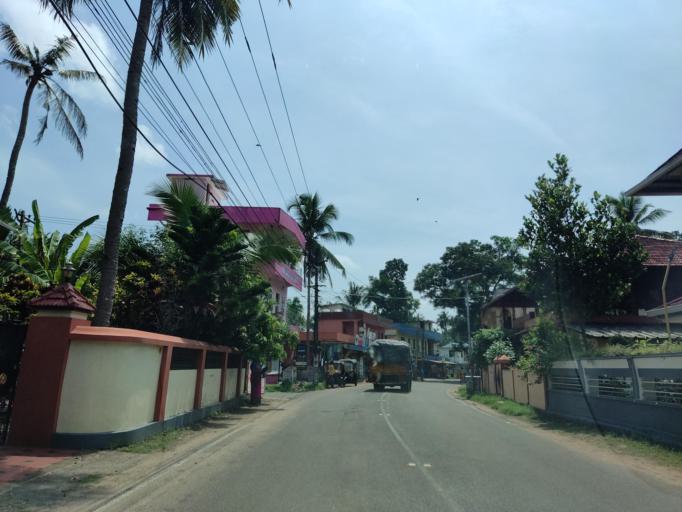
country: IN
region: Kerala
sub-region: Alappuzha
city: Chengannur
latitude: 9.3071
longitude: 76.5811
